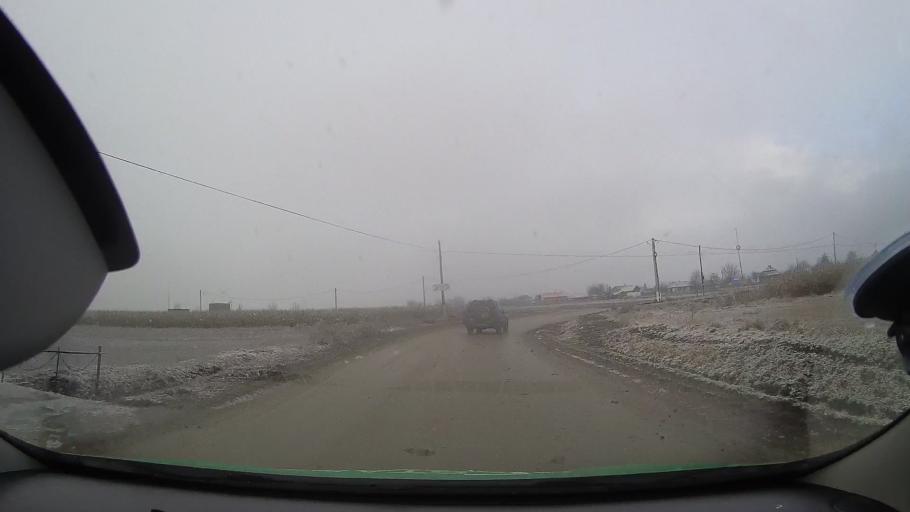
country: RO
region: Alba
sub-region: Comuna Noslac
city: Noslac
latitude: 46.3978
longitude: 23.9172
